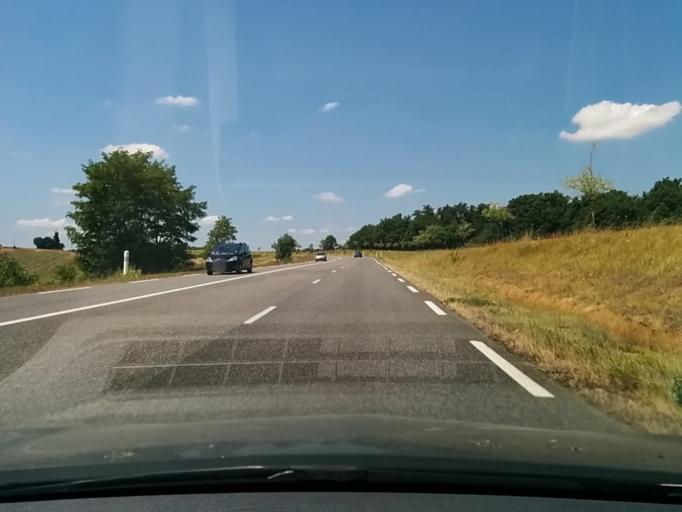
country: FR
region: Midi-Pyrenees
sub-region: Departement du Gers
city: Jegun
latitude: 43.7120
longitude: 0.4365
